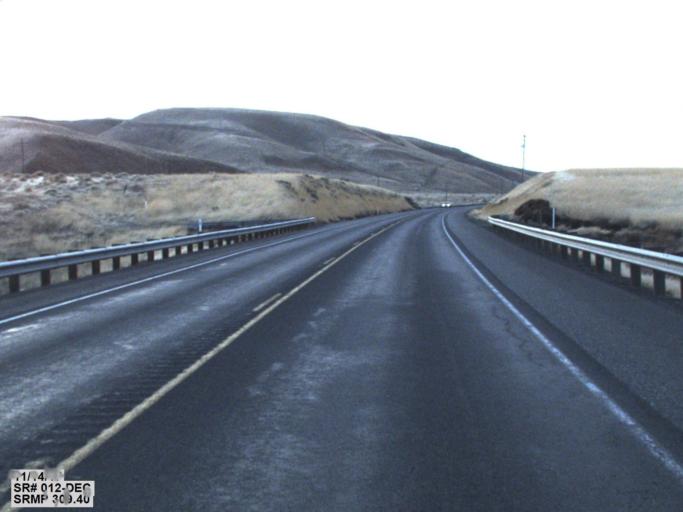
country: US
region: Washington
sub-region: Benton County
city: Finley
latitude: 46.0529
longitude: -118.8717
